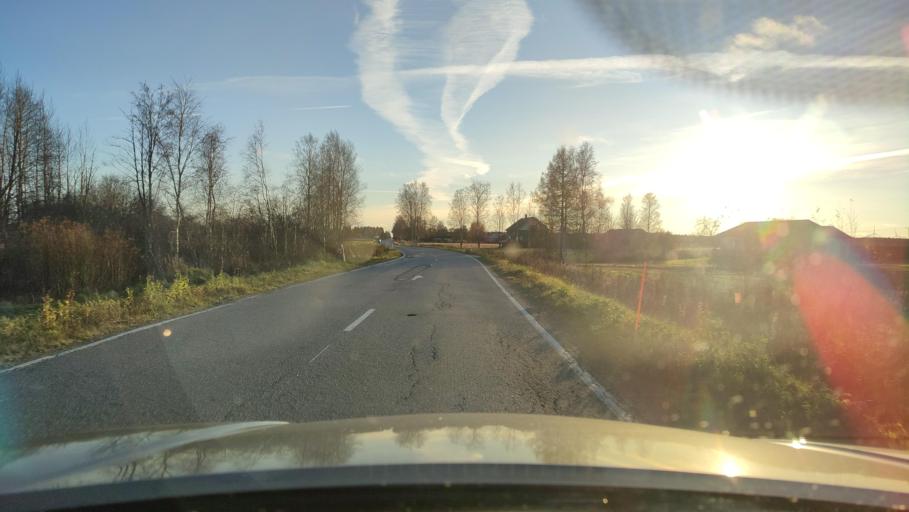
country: FI
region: Ostrobothnia
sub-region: Sydosterbotten
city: Naerpes
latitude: 62.6637
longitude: 21.5257
